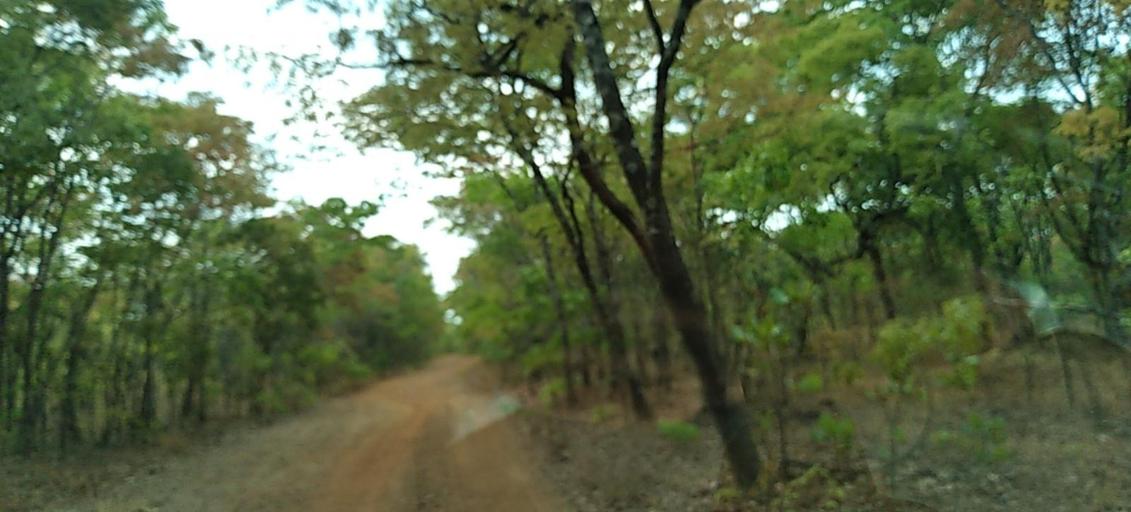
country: ZM
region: Copperbelt
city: Chililabombwe
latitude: -12.4962
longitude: 27.6395
